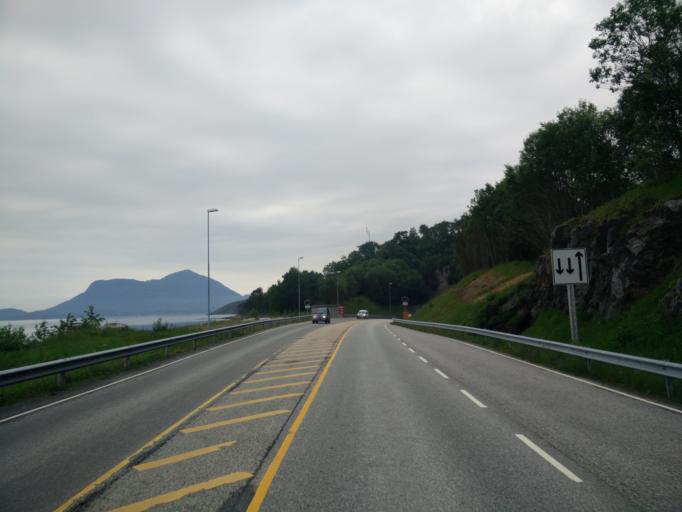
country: NO
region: More og Romsdal
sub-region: Kristiansund
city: Rensvik
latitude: 62.9802
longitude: 7.7946
